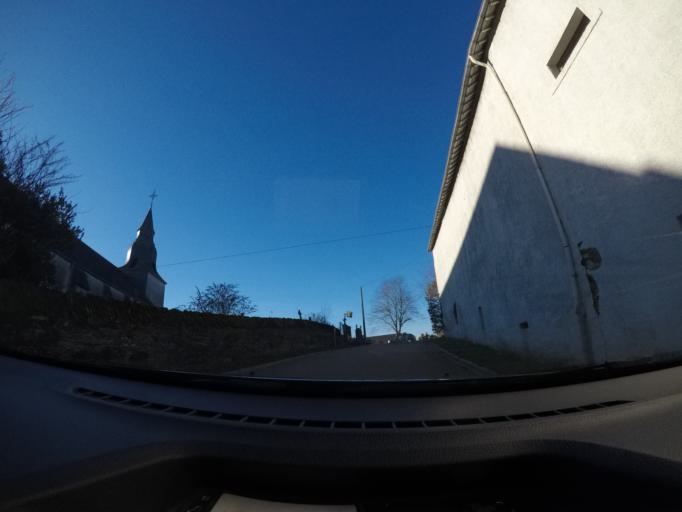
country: BE
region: Wallonia
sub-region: Province du Luxembourg
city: Bertrix
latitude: 49.8338
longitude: 5.3070
